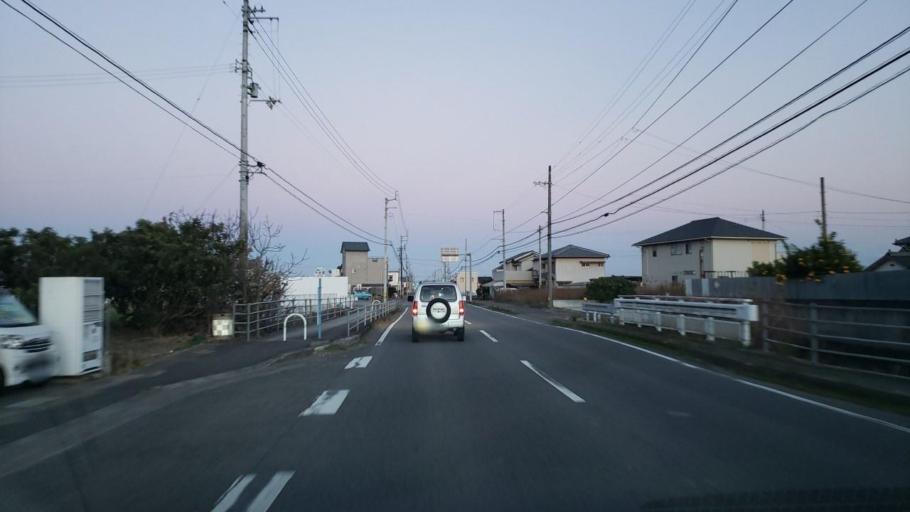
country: JP
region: Tokushima
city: Ishii
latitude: 34.1218
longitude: 134.4501
